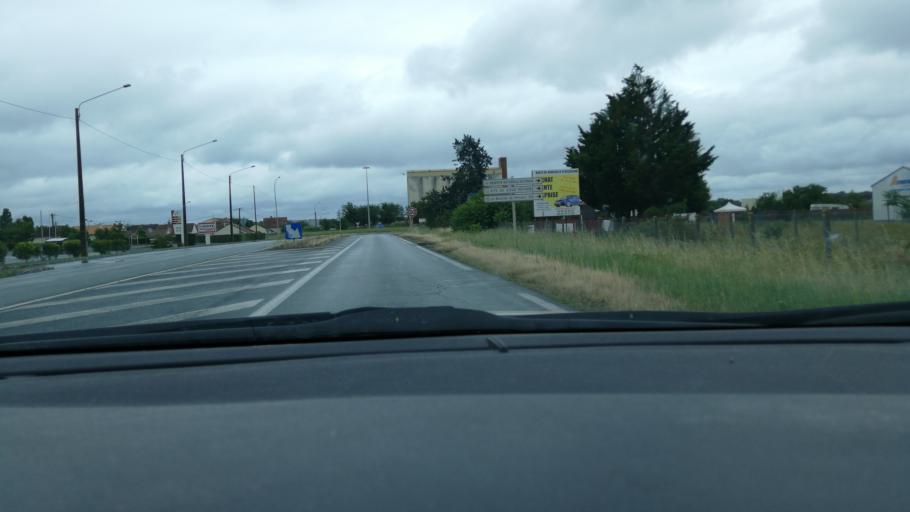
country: FR
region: Poitou-Charentes
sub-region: Departement de la Vienne
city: Naintre
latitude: 46.7555
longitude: 0.4857
